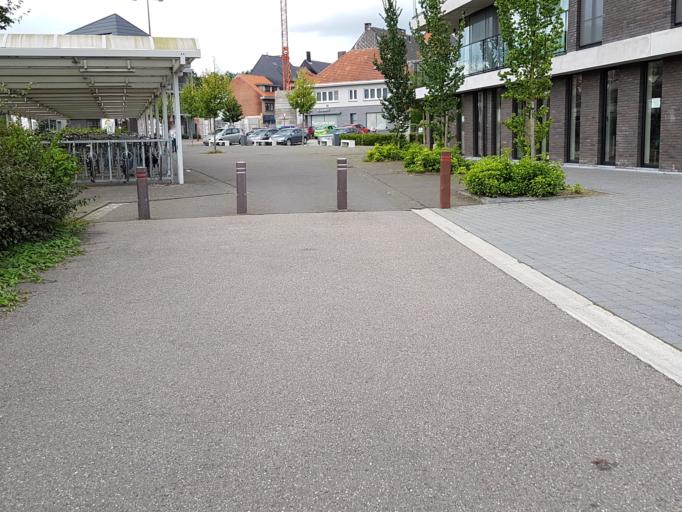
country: BE
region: Flanders
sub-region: Provincie Antwerpen
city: Kalmthout
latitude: 51.3639
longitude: 4.4604
